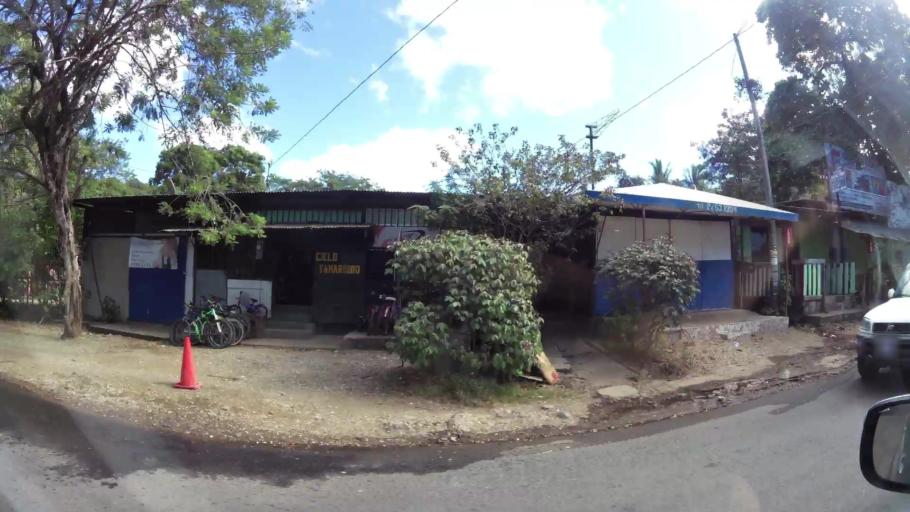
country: CR
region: Guanacaste
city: Santa Cruz
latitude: 10.3070
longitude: -85.8058
